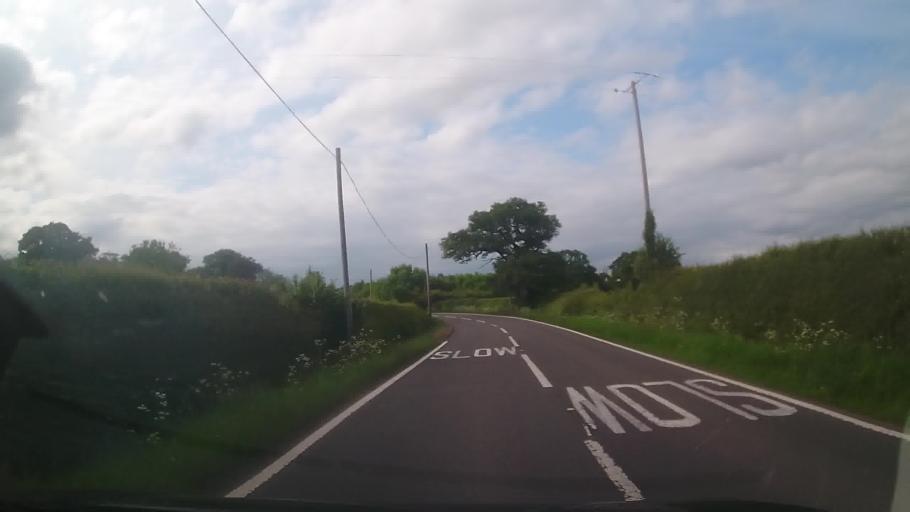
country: GB
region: England
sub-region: Shropshire
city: Petton
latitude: 52.8218
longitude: -2.7988
